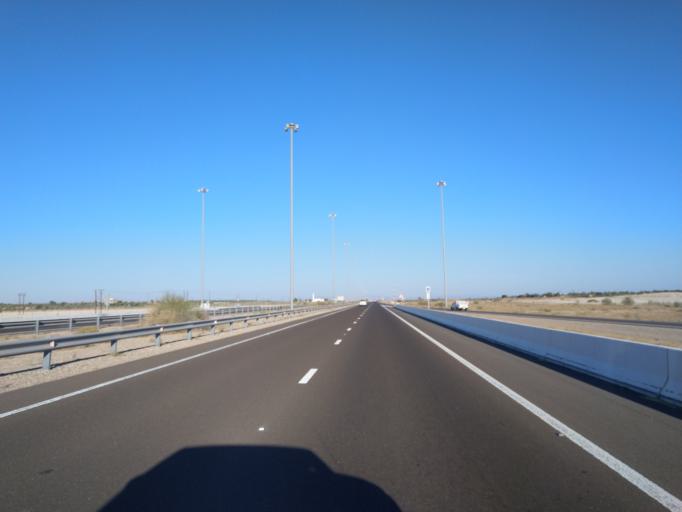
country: OM
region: Al Buraimi
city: Al Buraymi
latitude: 24.5383
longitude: 55.6070
